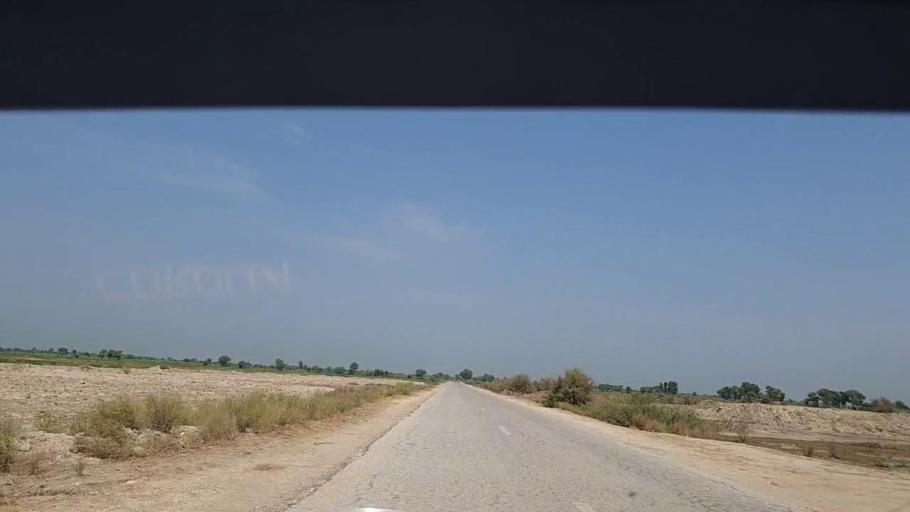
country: PK
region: Sindh
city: Thul
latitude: 28.1267
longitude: 68.8179
